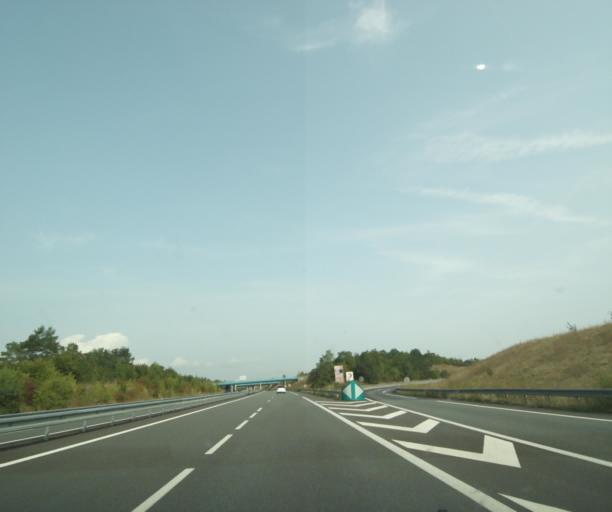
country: FR
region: Lower Normandy
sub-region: Departement de l'Orne
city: Valframbert
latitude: 48.4511
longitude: 0.1327
